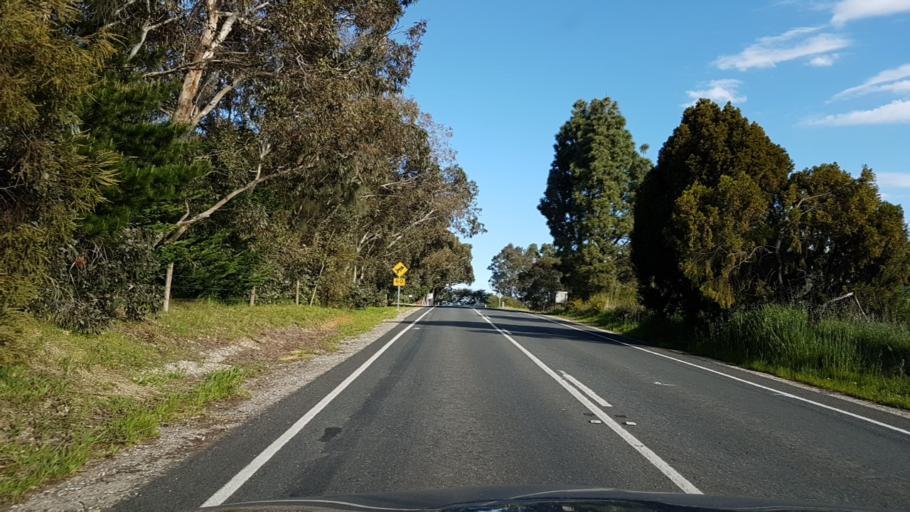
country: AU
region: South Australia
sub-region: Adelaide Hills
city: Lobethal
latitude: -34.8767
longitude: 138.8912
